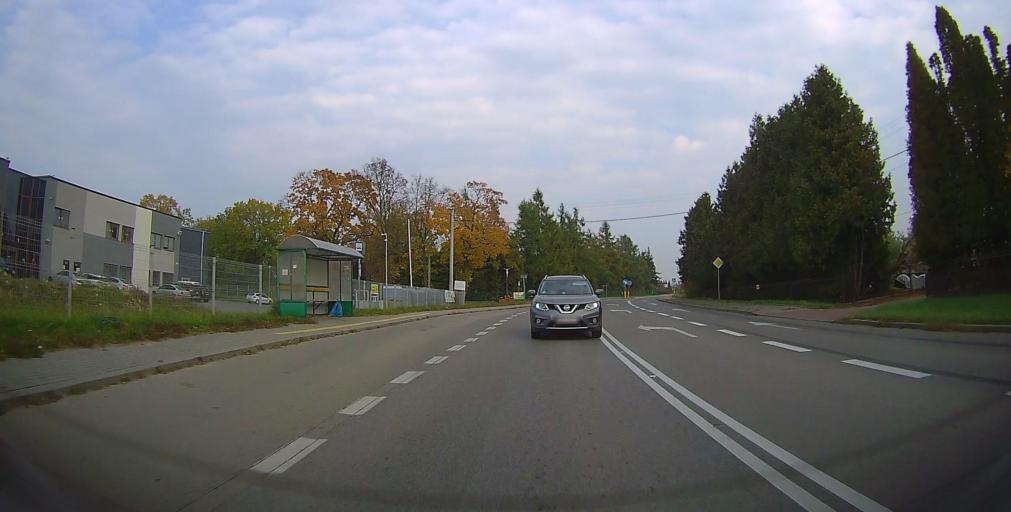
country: PL
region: Masovian Voivodeship
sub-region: Powiat grojecki
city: Belsk Duzy
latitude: 51.7757
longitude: 20.7700
